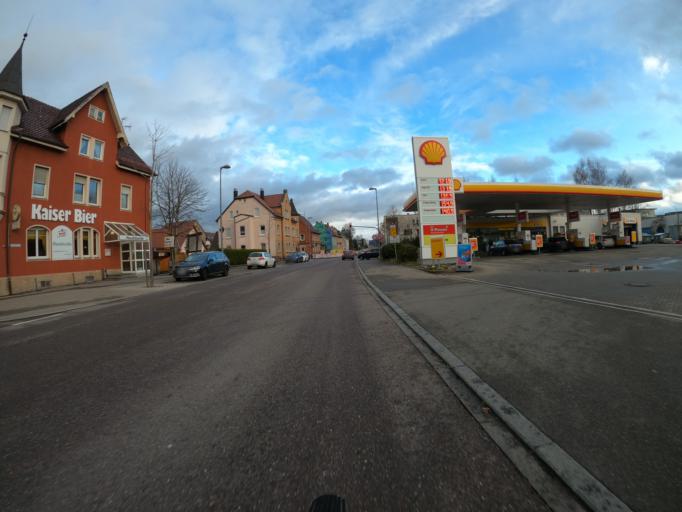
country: DE
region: Baden-Wuerttemberg
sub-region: Regierungsbezirk Stuttgart
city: Eislingen
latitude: 48.6935
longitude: 9.7096
